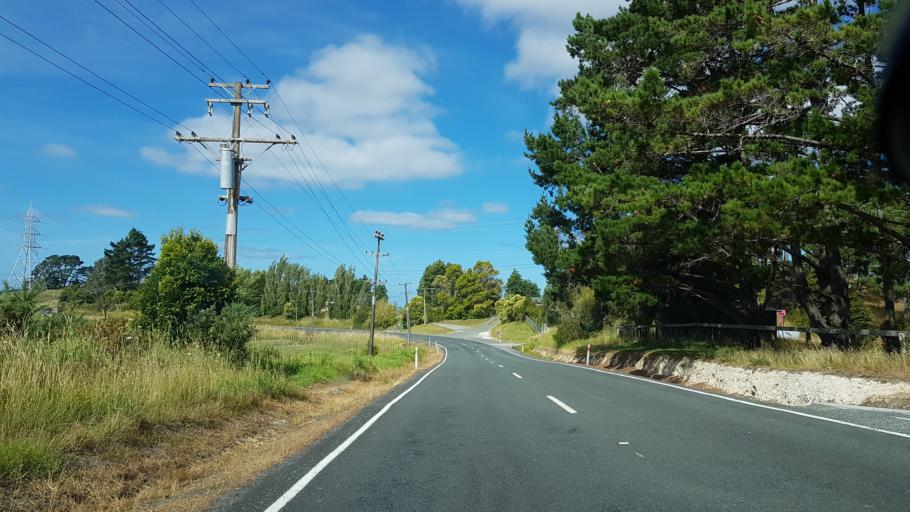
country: NZ
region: Auckland
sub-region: Auckland
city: Rothesay Bay
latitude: -36.6915
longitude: 174.6788
